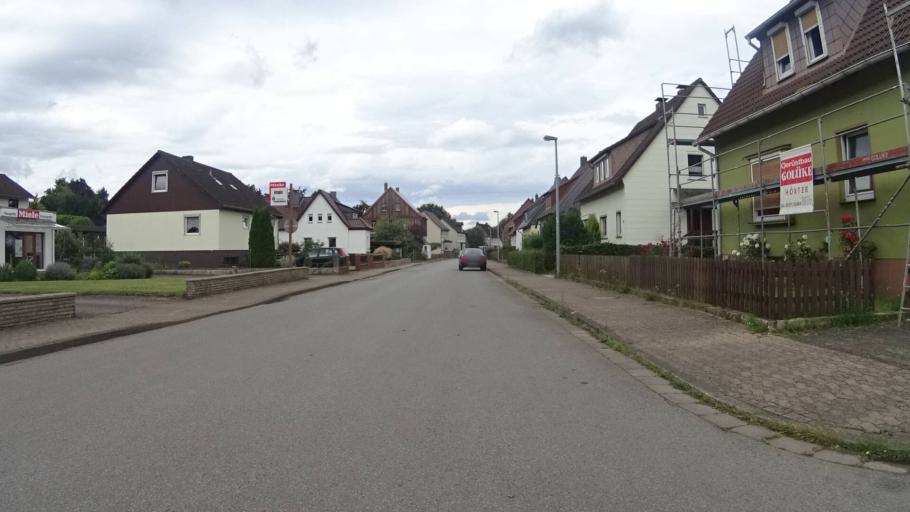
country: DE
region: Lower Saxony
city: Bevern
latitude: 51.8554
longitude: 9.5052
